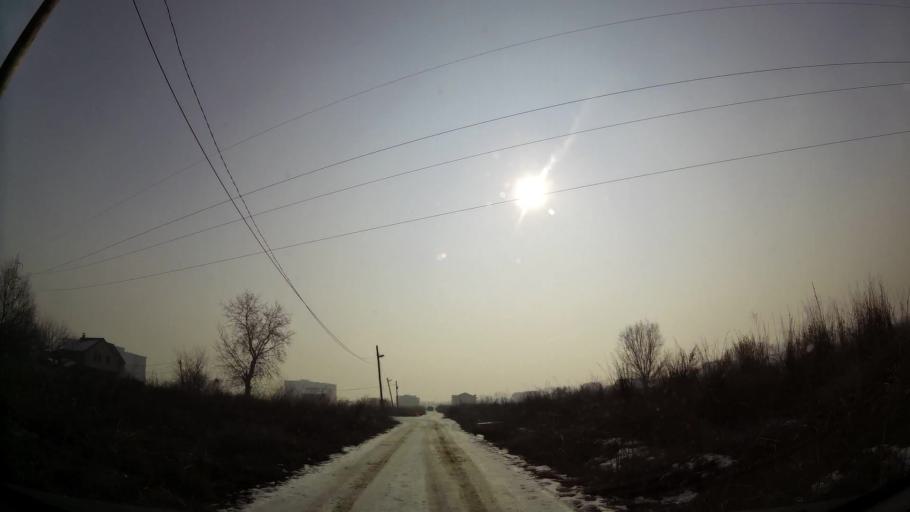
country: MK
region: Kisela Voda
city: Kisela Voda
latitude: 41.9955
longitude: 21.5171
